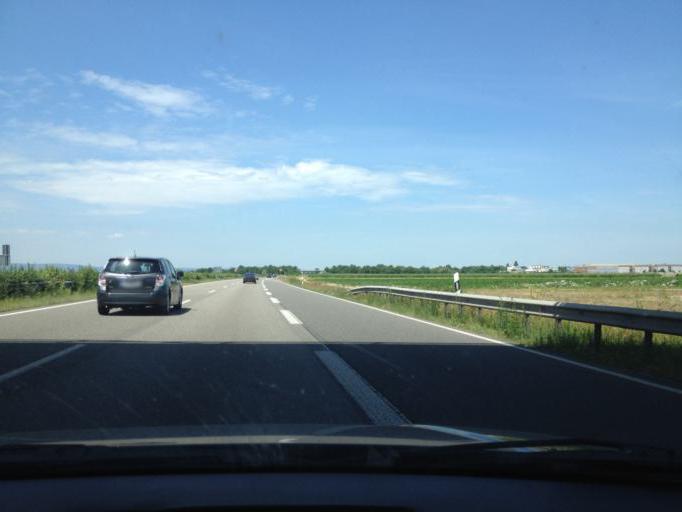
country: DE
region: Rheinland-Pfalz
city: Limburgerhof
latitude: 49.4380
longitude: 8.3841
